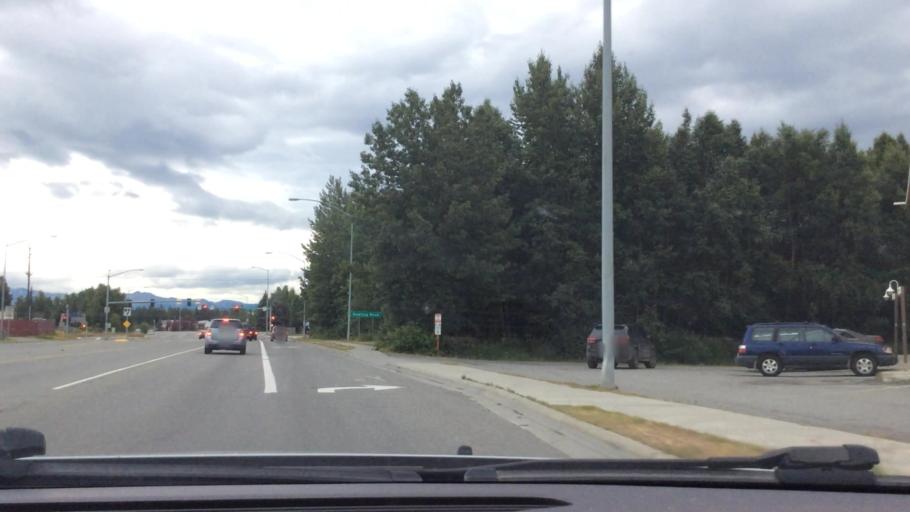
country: US
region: Alaska
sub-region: Anchorage Municipality
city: Anchorage
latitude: 61.1682
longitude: -149.8383
